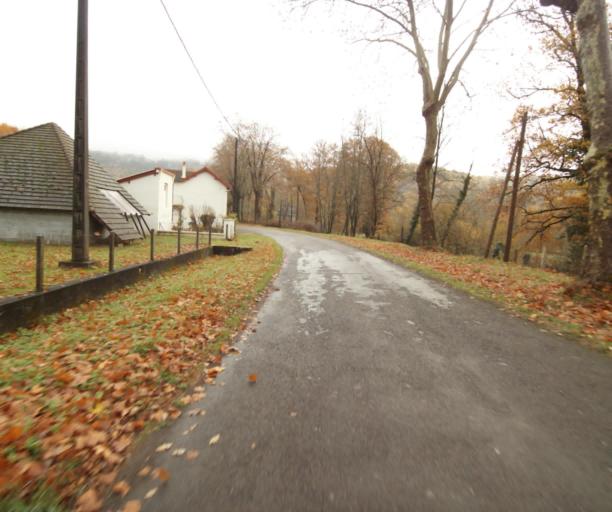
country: FR
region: Limousin
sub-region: Departement de la Correze
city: Cornil
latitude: 45.1796
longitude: 1.6505
